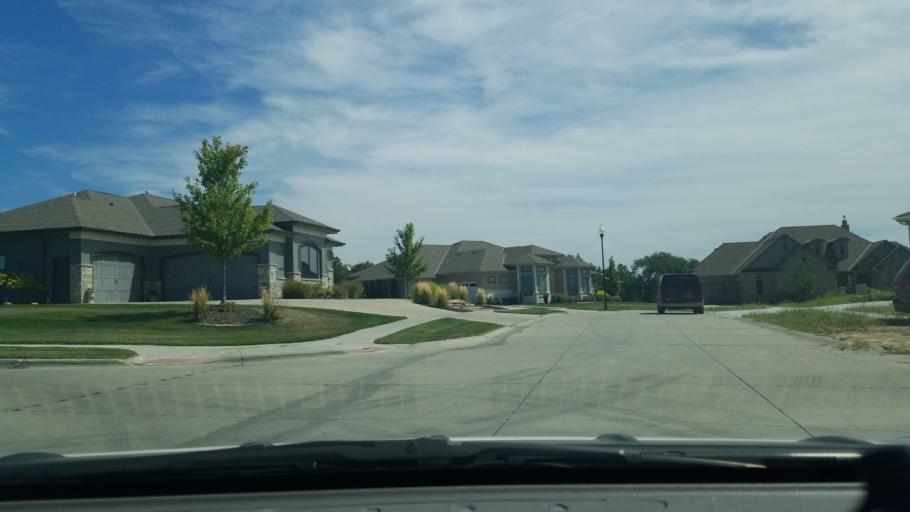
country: US
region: Nebraska
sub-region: Sarpy County
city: Papillion
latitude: 41.1431
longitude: -96.1019
